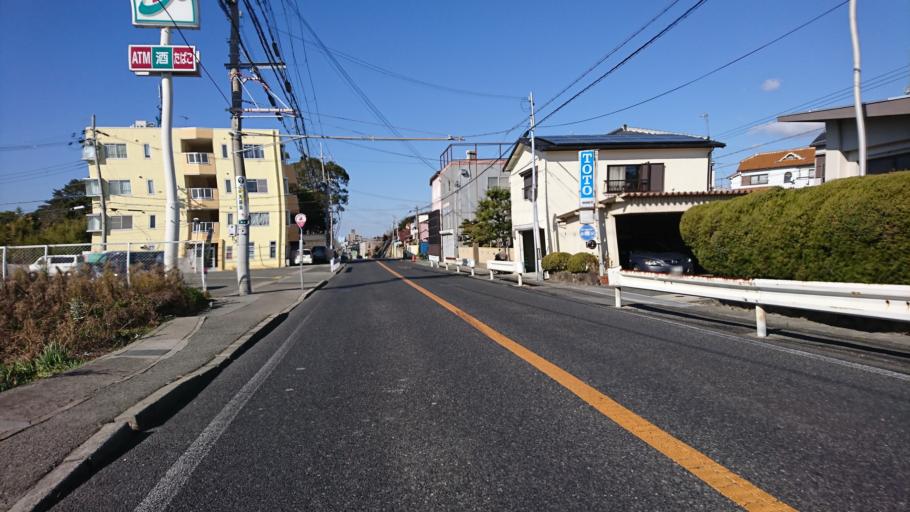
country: JP
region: Hyogo
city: Akashi
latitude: 34.6647
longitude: 134.9451
